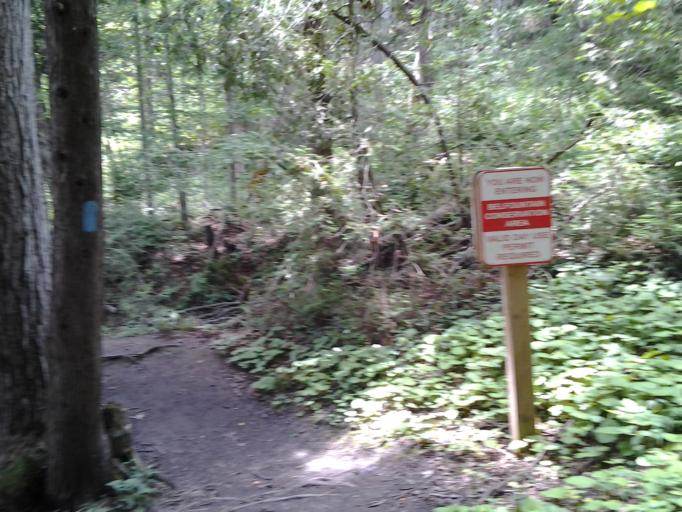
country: CA
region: Ontario
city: Orangeville
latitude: 43.7961
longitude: -80.0099
